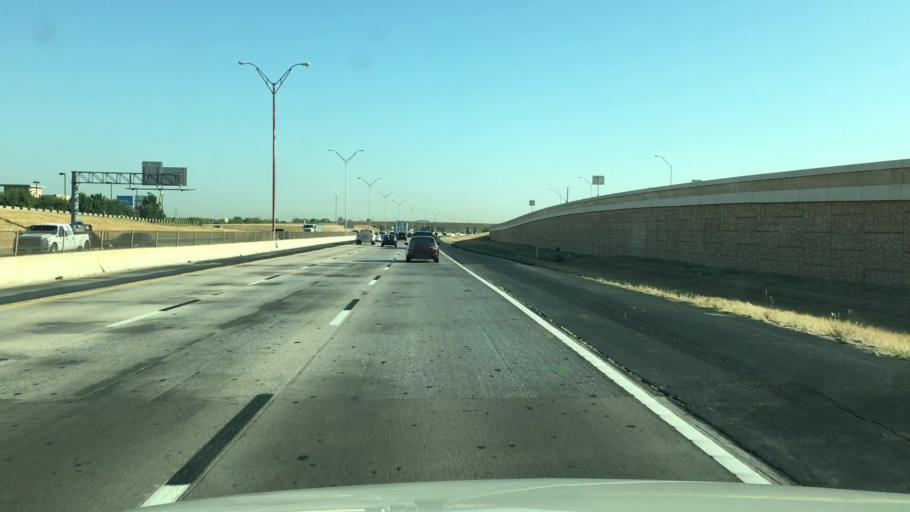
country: US
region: Texas
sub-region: Johnson County
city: Burleson
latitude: 32.5725
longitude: -97.3190
